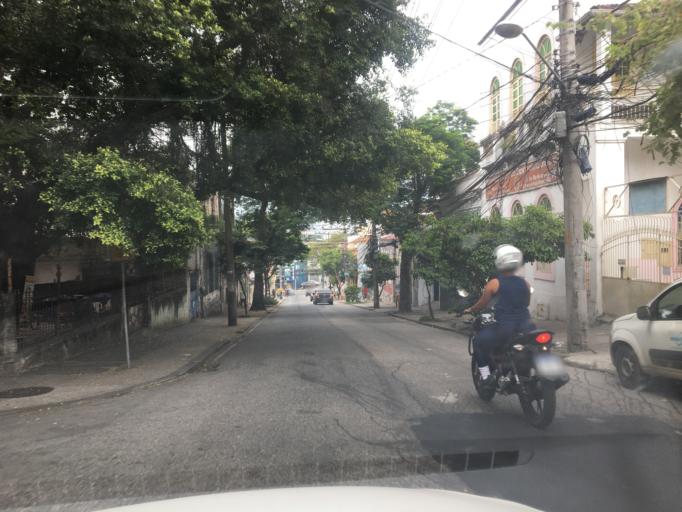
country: BR
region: Rio de Janeiro
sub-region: Rio De Janeiro
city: Rio de Janeiro
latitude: -22.8983
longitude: -43.2278
